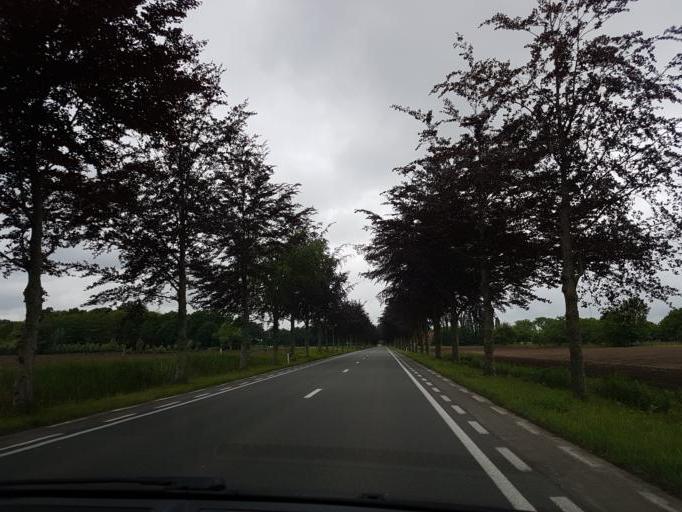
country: BE
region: Flanders
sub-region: Provincie West-Vlaanderen
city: Beernem
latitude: 51.1236
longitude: 3.3606
